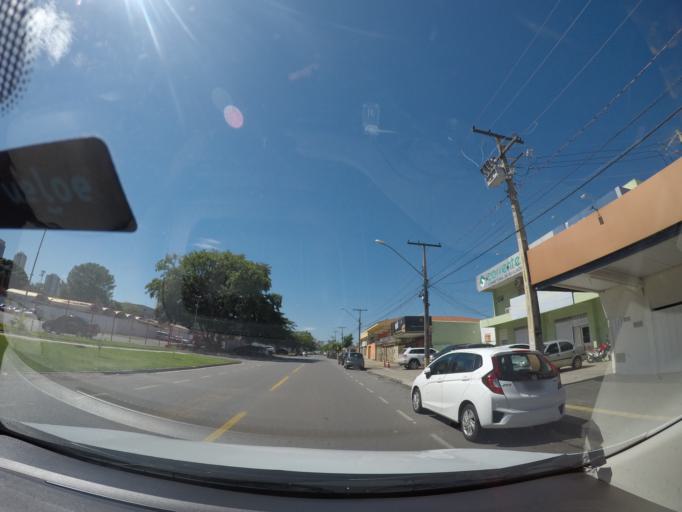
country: BR
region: Goias
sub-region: Goiania
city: Goiania
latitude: -16.7012
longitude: -49.2820
